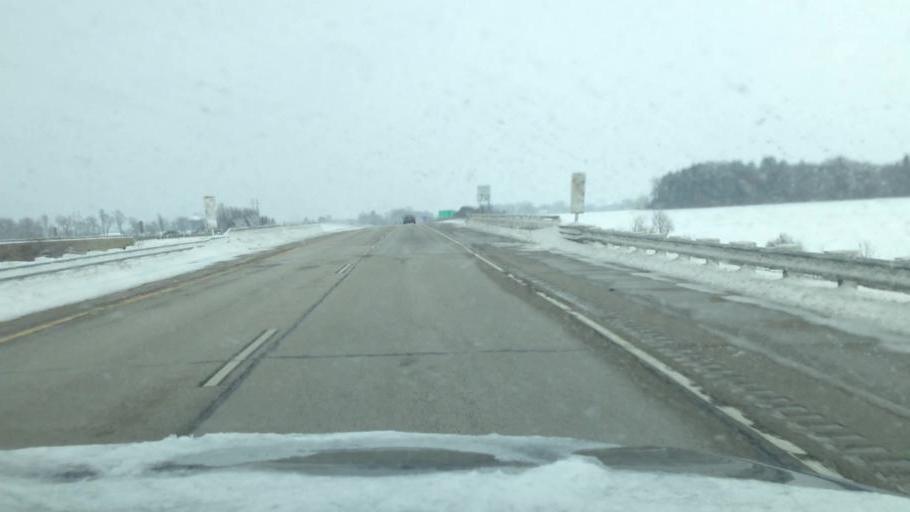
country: US
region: Wisconsin
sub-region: Walworth County
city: Elkhorn
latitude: 42.6986
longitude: -88.4939
